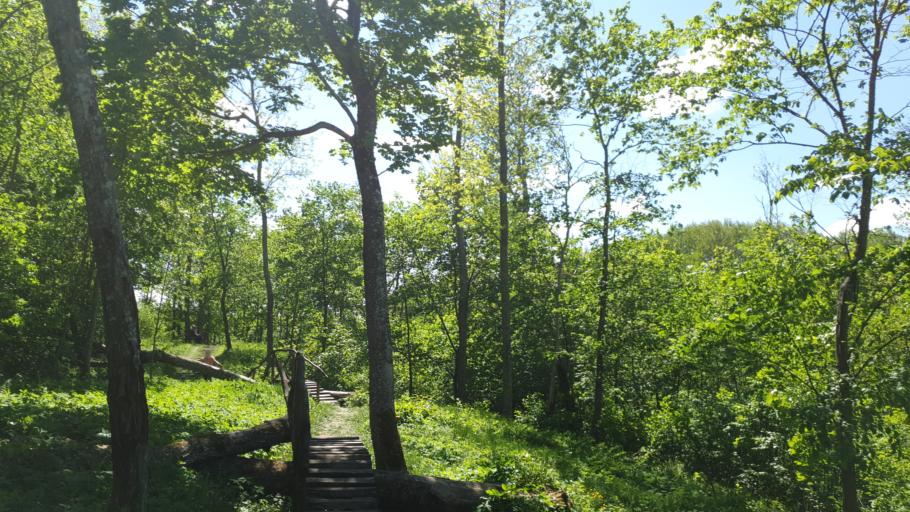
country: LT
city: Moletai
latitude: 55.0729
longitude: 25.4153
